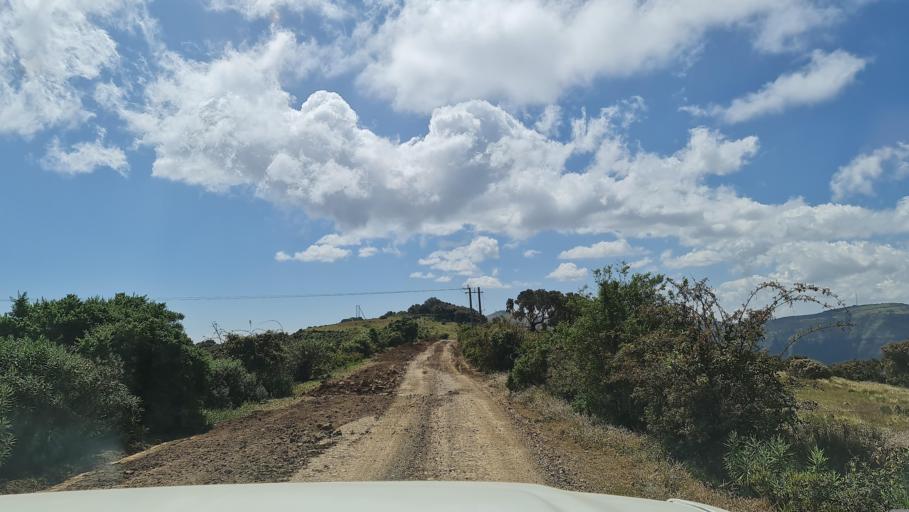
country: ET
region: Amhara
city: Debark'
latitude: 13.2336
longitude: 38.0184
